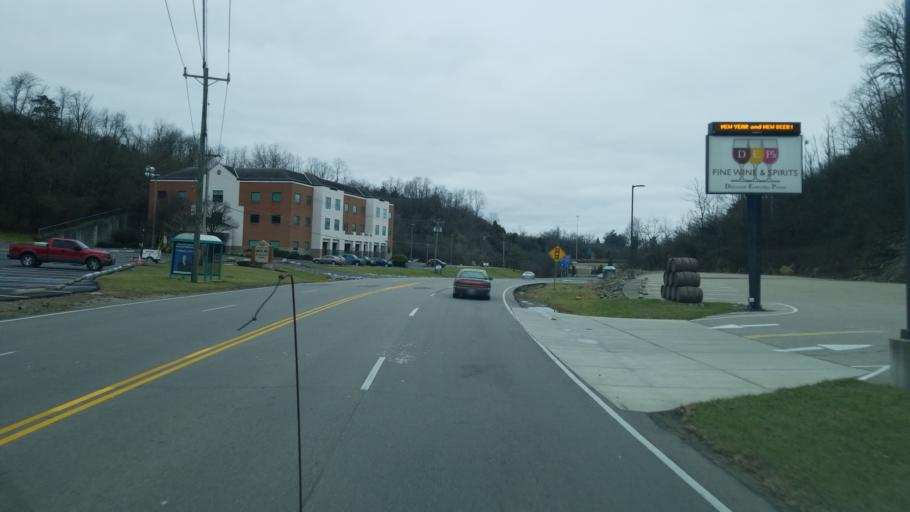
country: US
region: Kentucky
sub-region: Campbell County
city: Southgate
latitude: 39.0644
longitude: -84.4610
